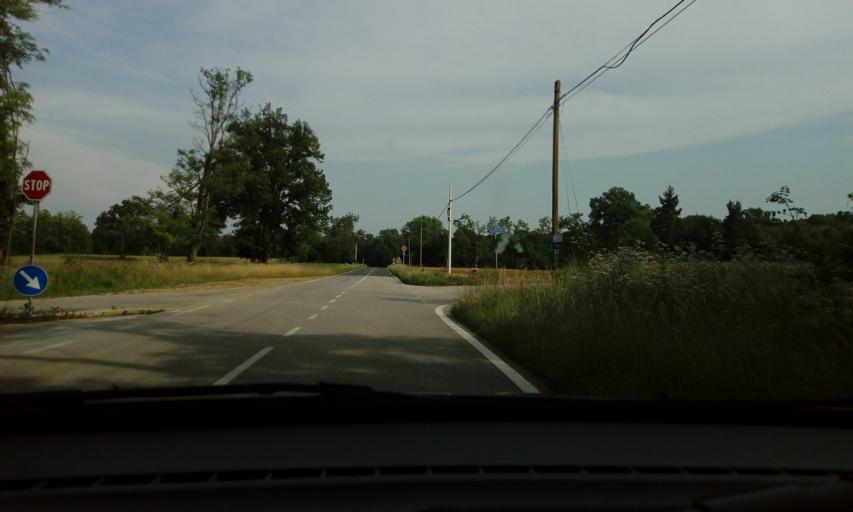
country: IT
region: Friuli Venezia Giulia
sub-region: Provincia di Udine
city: Rive d'Arcano
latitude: 46.1337
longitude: 13.0602
